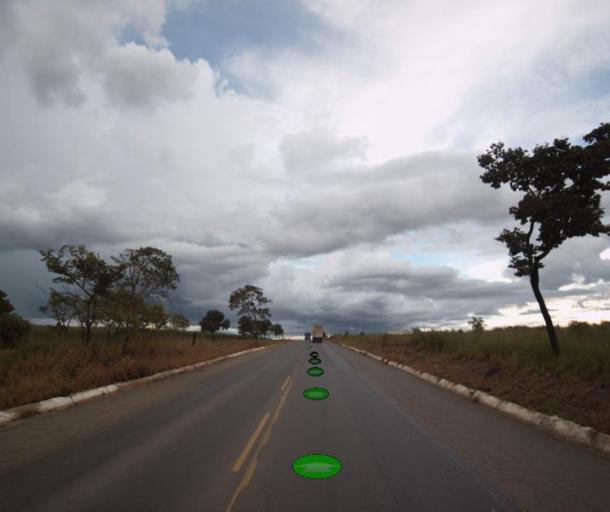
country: BR
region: Goias
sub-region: Itapaci
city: Itapaci
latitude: -14.8036
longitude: -49.2869
